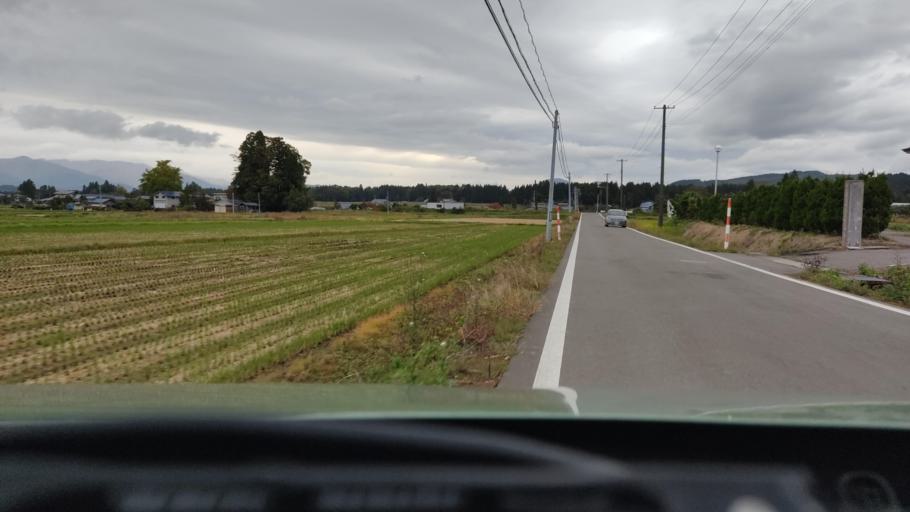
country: JP
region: Akita
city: Kakunodatemachi
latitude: 39.5642
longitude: 140.6108
